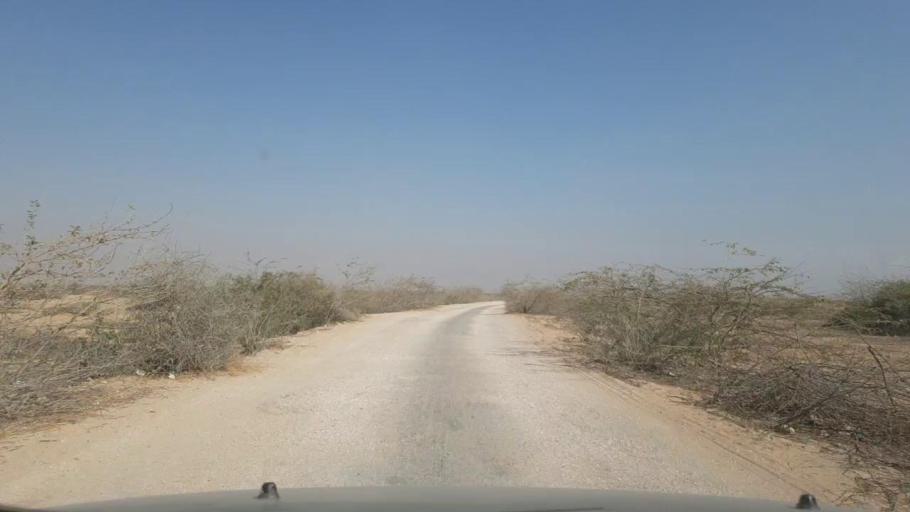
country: PK
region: Sindh
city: Thatta
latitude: 24.9311
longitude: 67.9395
